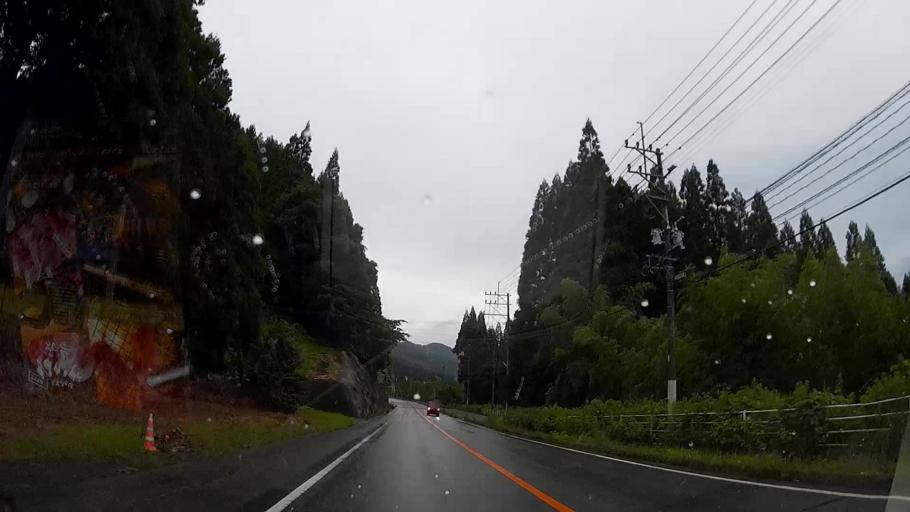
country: JP
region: Oita
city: Tsukawaki
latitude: 33.1446
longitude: 131.0591
